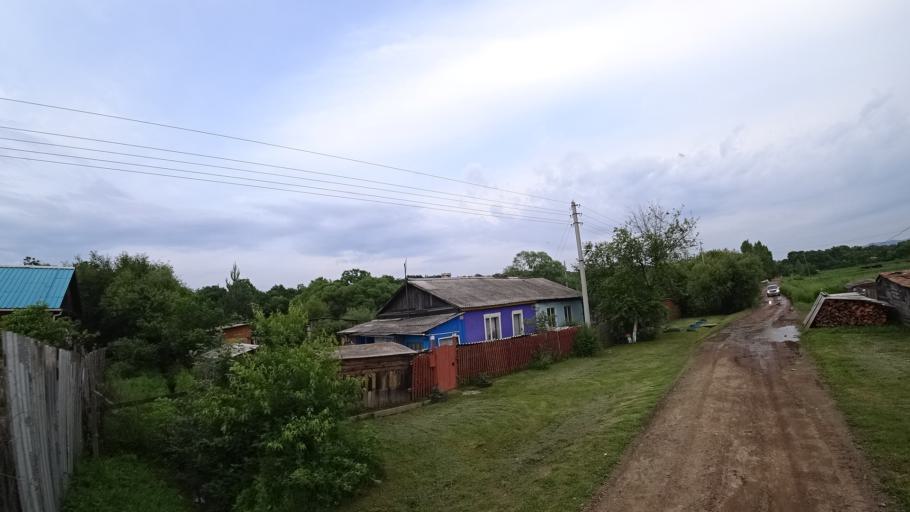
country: RU
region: Primorskiy
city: Novosysoyevka
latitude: 44.2369
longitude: 133.3794
